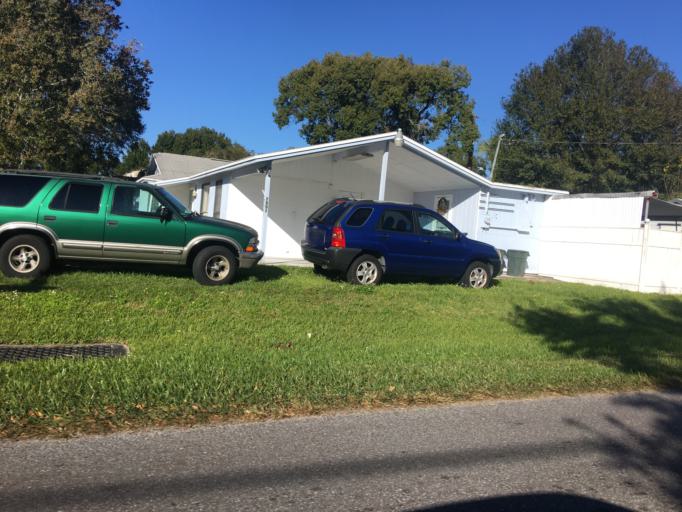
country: US
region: Florida
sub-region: Hillsborough County
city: Egypt Lake-Leto
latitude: 28.0181
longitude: -82.4960
